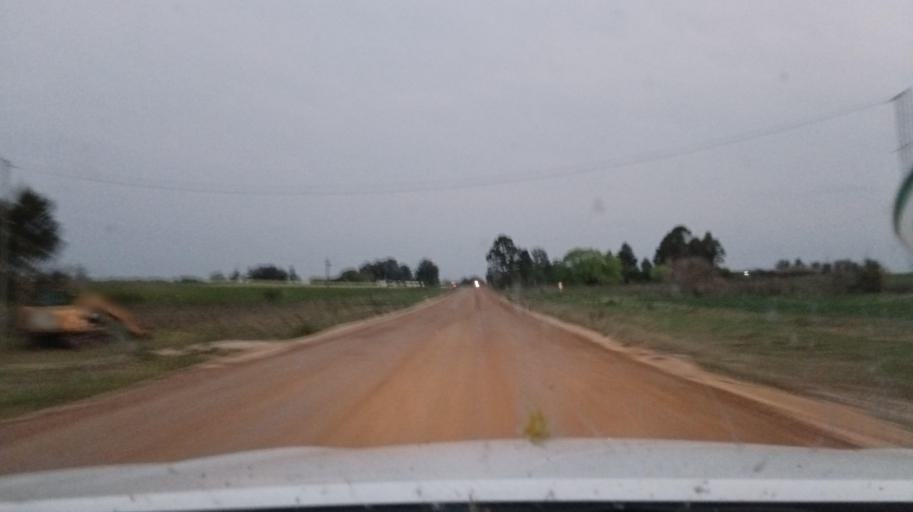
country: UY
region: Canelones
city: Santa Rosa
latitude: -34.5484
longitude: -56.1021
